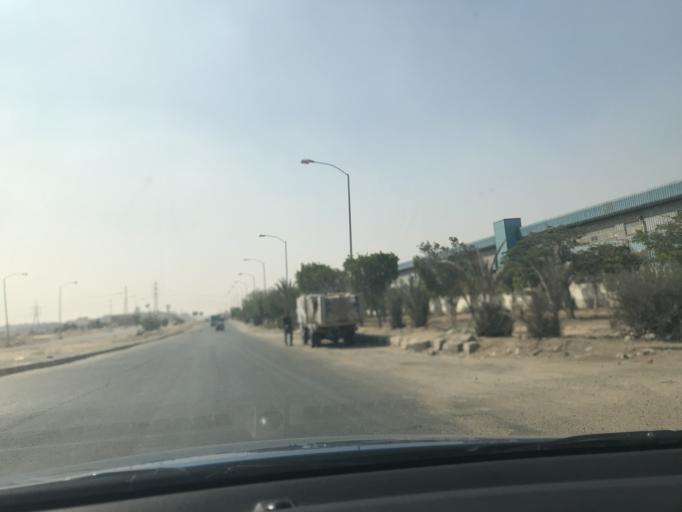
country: EG
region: Eastern Province
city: Bilbays
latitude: 30.2509
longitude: 31.7587
